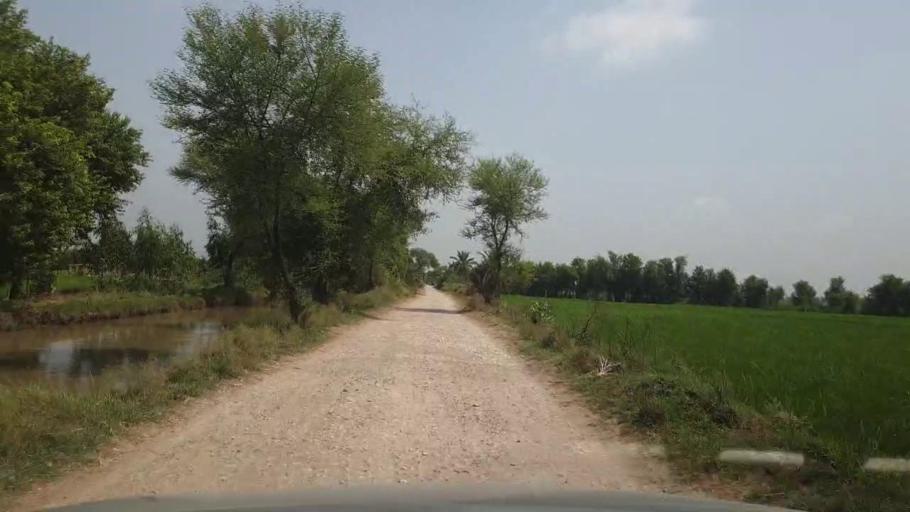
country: PK
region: Sindh
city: Garhi Yasin
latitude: 27.9438
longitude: 68.3732
